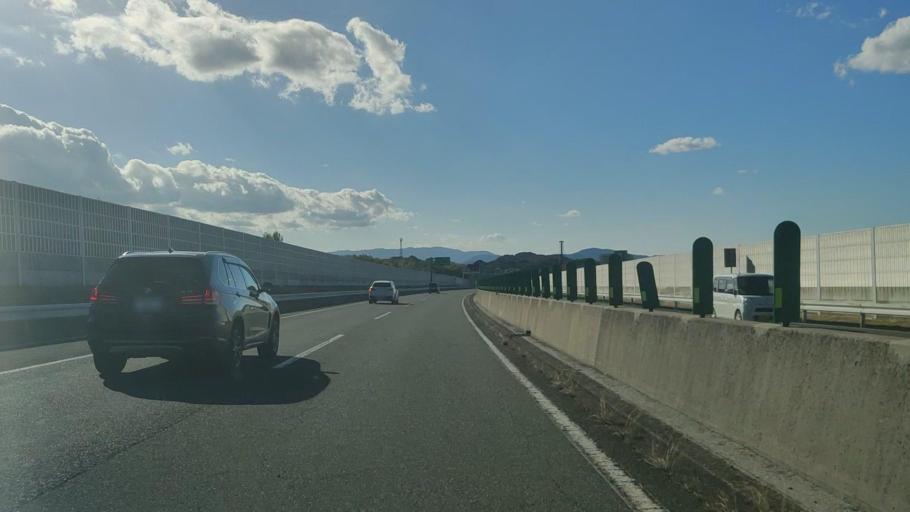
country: JP
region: Fukuoka
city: Nakama
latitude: 33.8205
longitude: 130.7577
